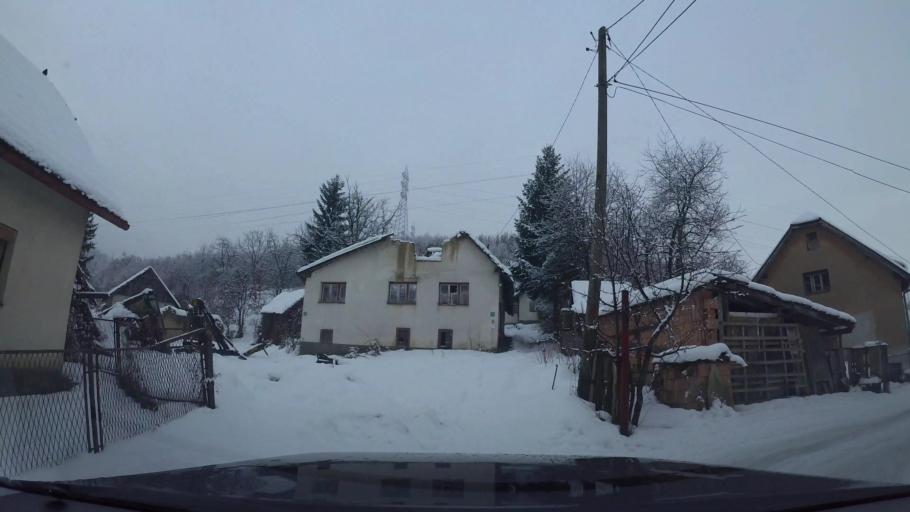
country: BA
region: Federation of Bosnia and Herzegovina
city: Vogosca
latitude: 43.8831
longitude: 18.3221
